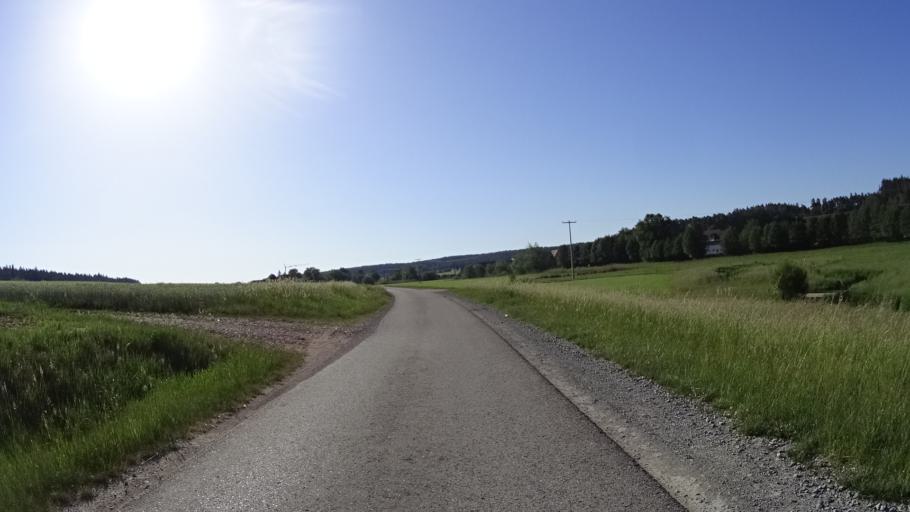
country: DE
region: Bavaria
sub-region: Regierungsbezirk Mittelfranken
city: Wieseth
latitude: 49.1587
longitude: 10.5069
